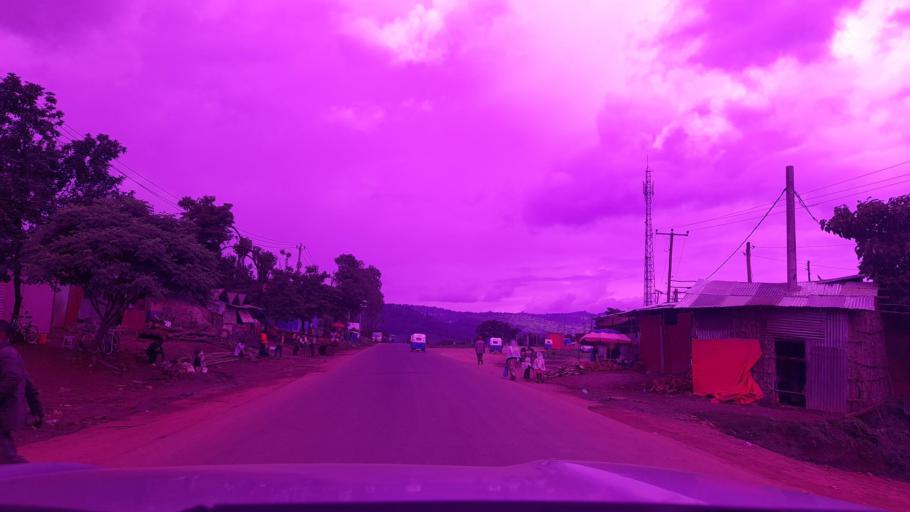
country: ET
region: Oromiya
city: Jima
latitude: 7.6704
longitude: 36.8566
